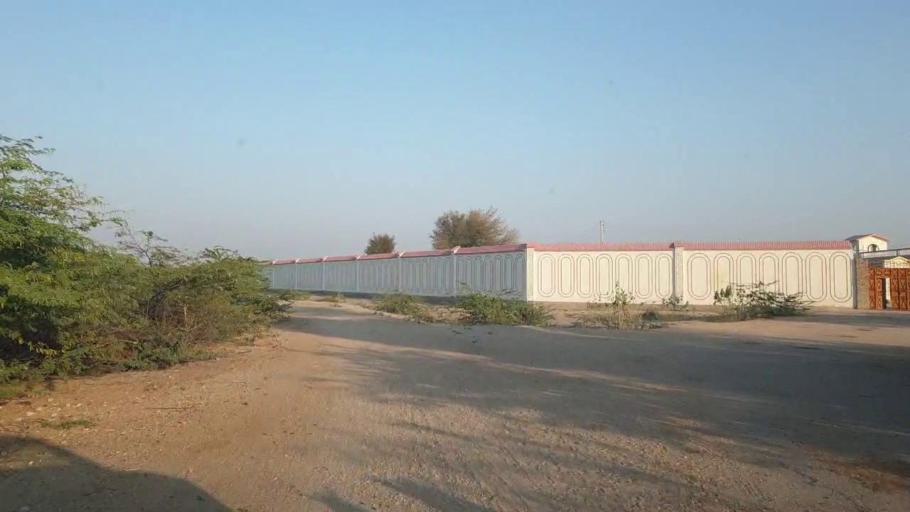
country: PK
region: Sindh
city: Chor
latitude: 25.5344
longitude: 69.8067
